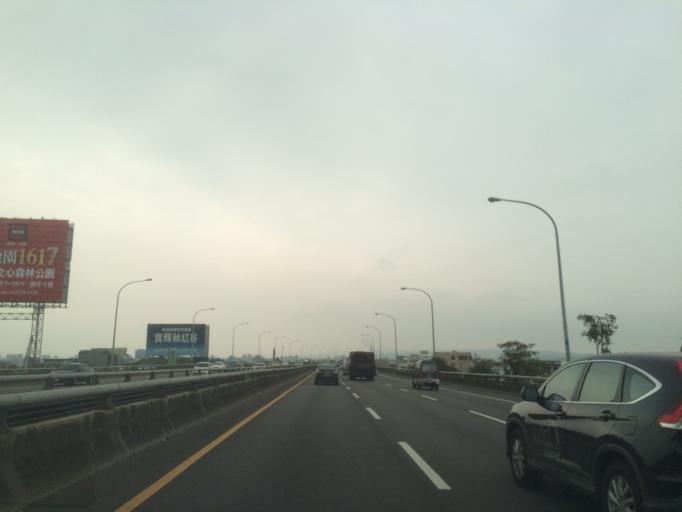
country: TW
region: Taiwan
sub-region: Taichung City
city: Taichung
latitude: 24.1413
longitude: 120.6228
